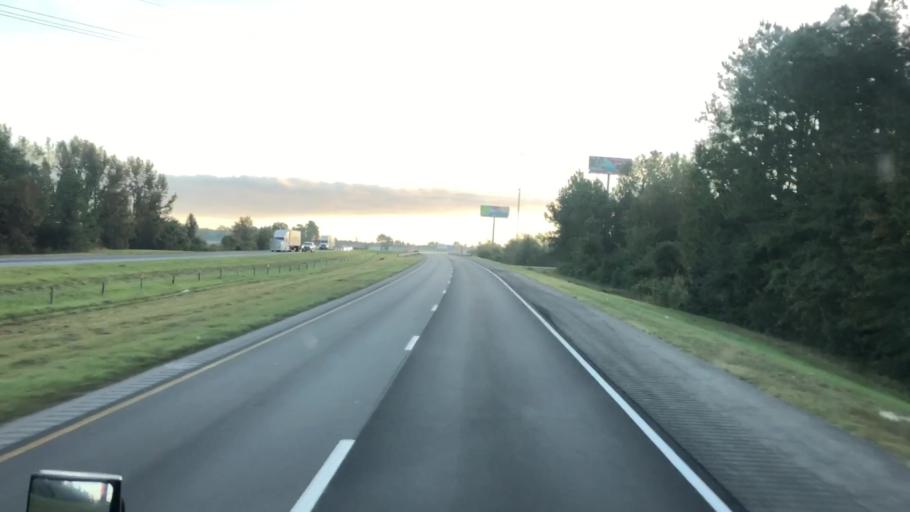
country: US
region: South Carolina
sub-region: Clarendon County
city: Manning
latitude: 33.5970
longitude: -80.3336
